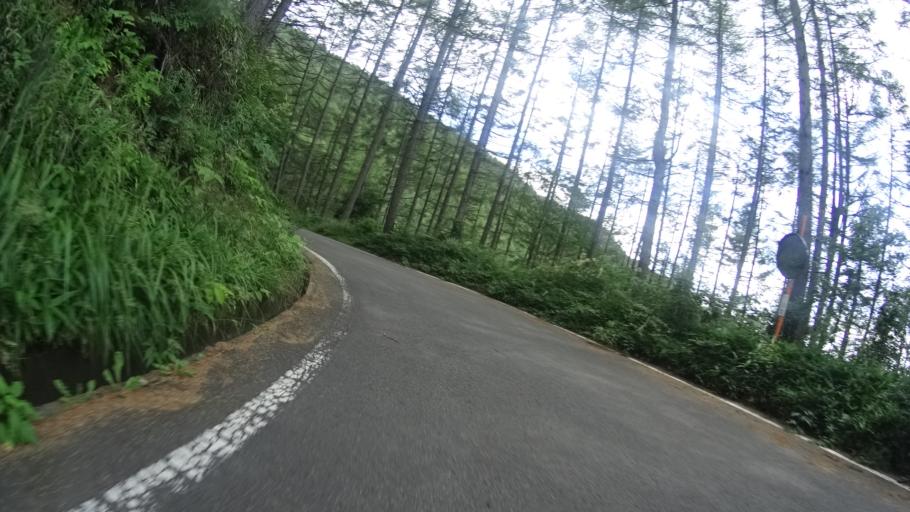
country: JP
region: Yamanashi
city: Enzan
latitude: 35.8369
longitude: 138.6396
